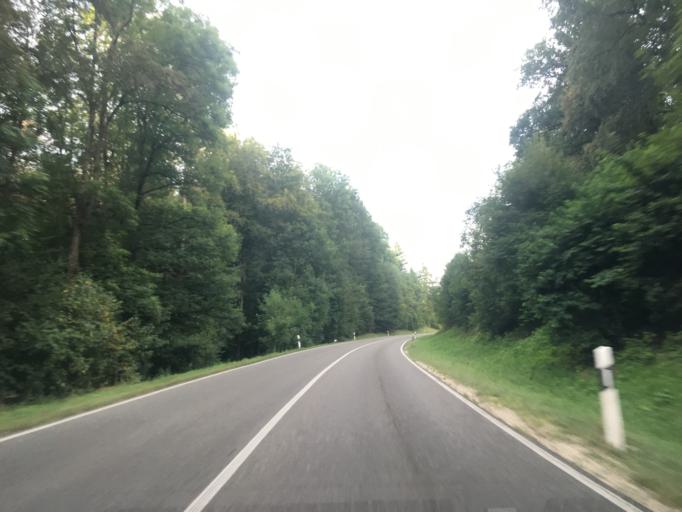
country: DE
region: Baden-Wuerttemberg
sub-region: Tuebingen Region
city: Eningen unter Achalm
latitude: 48.5092
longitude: 9.2652
